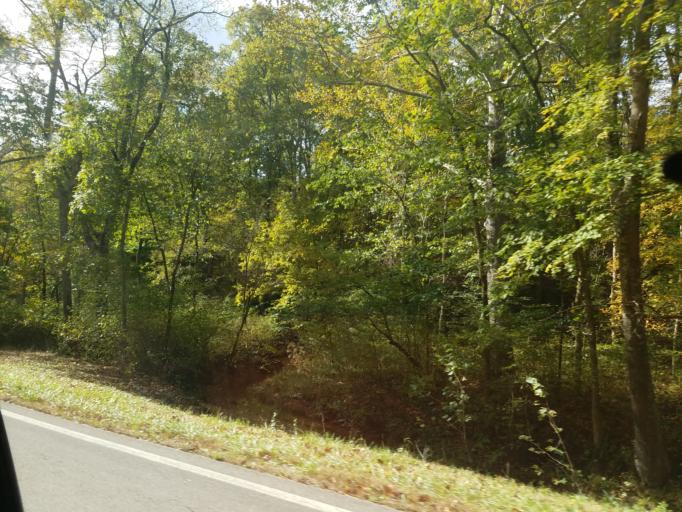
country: US
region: Ohio
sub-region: Vinton County
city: McArthur
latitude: 39.1698
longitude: -82.4396
